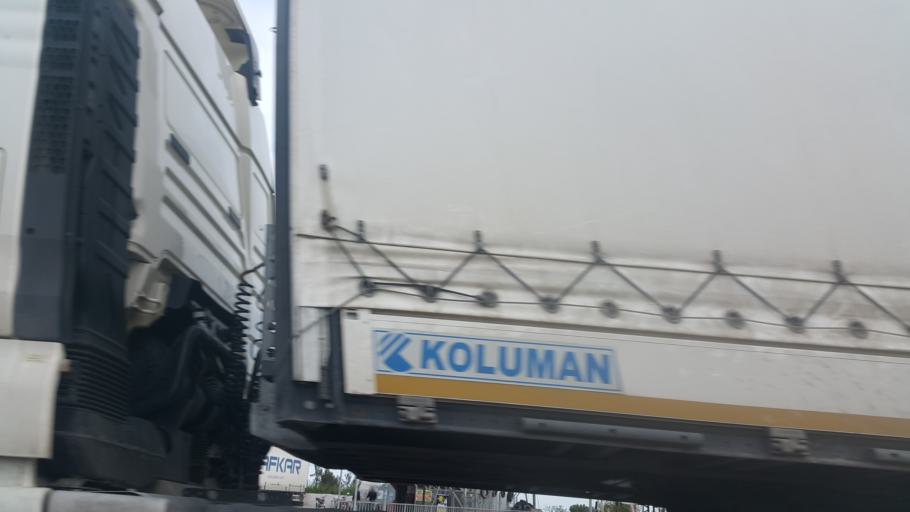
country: TR
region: Mersin
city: Yenice
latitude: 36.9559
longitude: 35.0026
